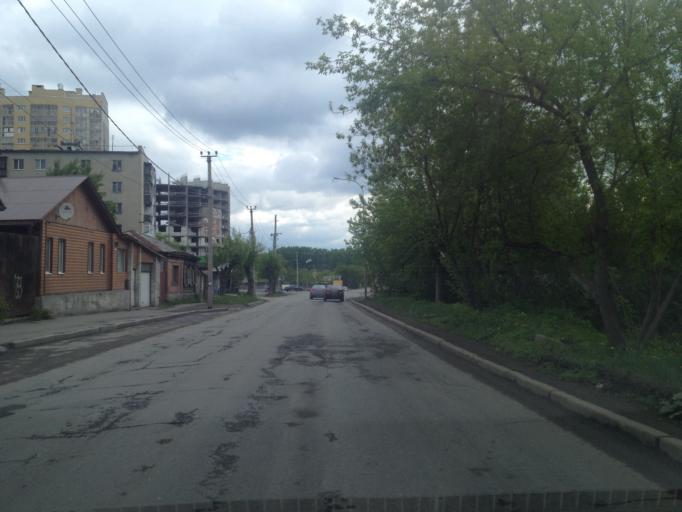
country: RU
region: Sverdlovsk
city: Yekaterinburg
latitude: 56.7810
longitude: 60.6533
